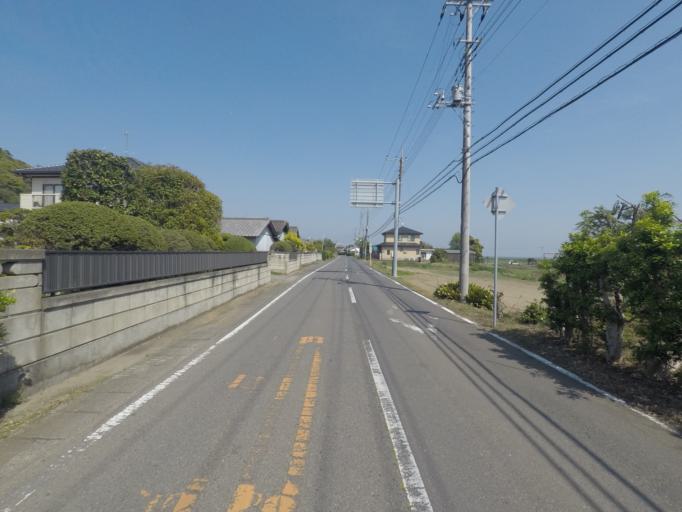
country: JP
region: Ibaraki
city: Inashiki
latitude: 36.0631
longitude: 140.3293
